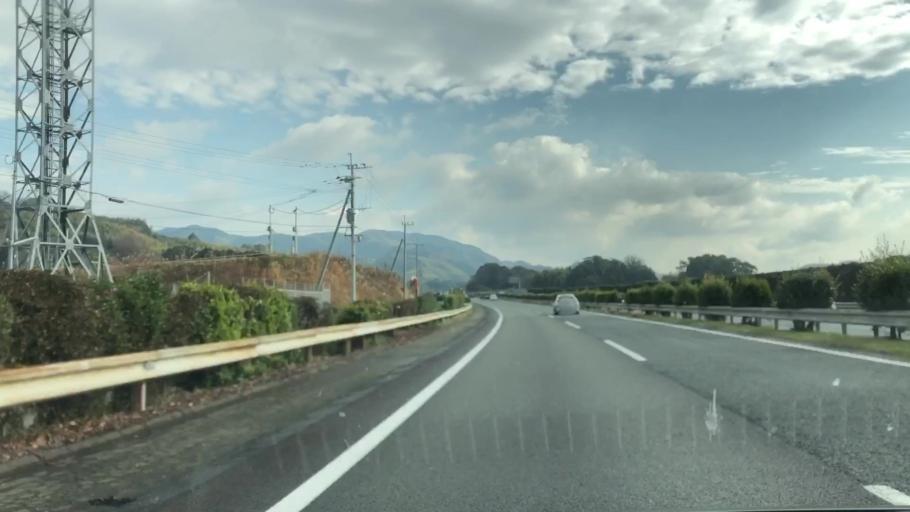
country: JP
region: Fukuoka
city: Setakamachi-takayanagi
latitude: 33.1211
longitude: 130.5213
